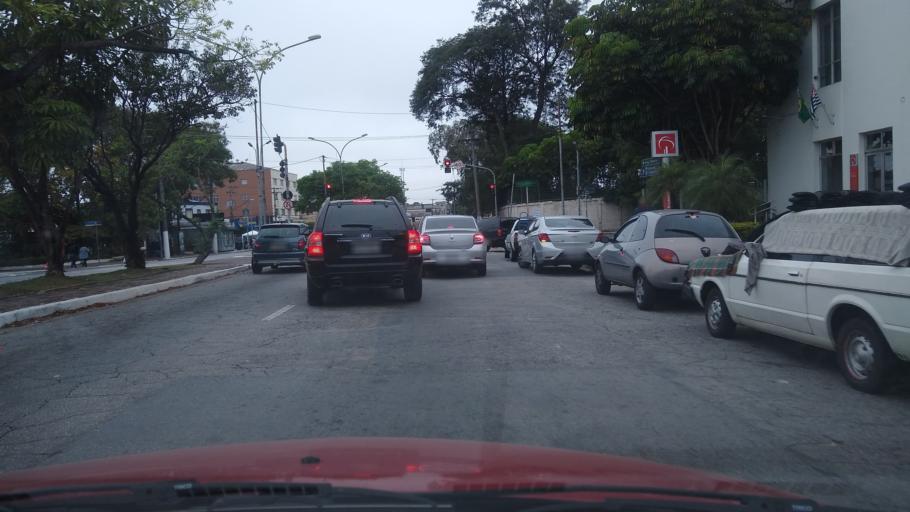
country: BR
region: Sao Paulo
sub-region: Diadema
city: Diadema
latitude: -23.6246
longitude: -46.6197
